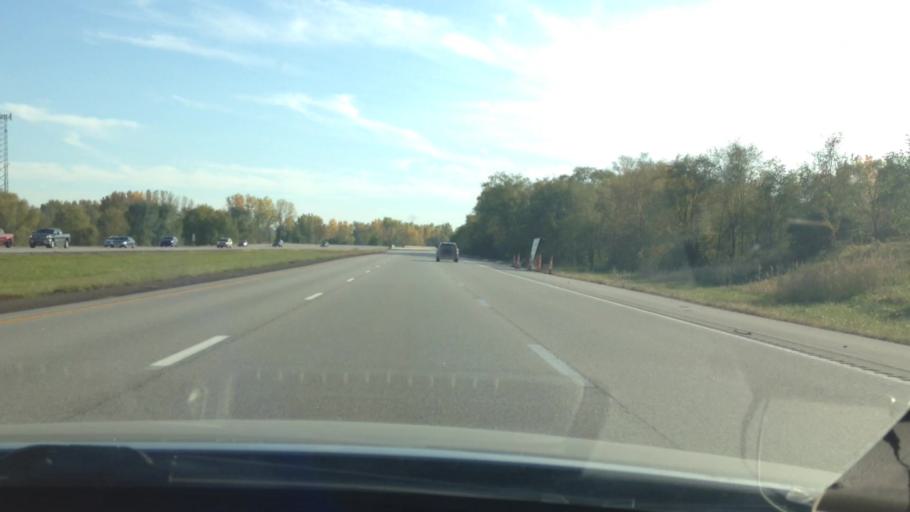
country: US
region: Missouri
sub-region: Platte County
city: Weatherby Lake
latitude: 39.1995
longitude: -94.7617
